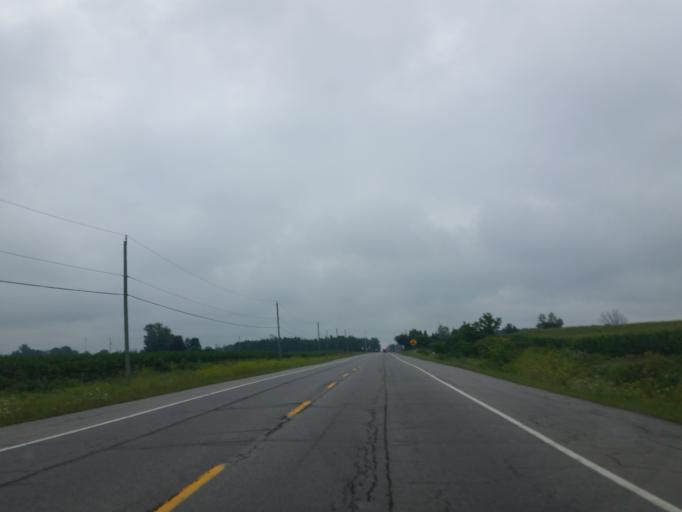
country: CA
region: Ontario
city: Clarence-Rockland
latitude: 45.3491
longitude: -75.3676
